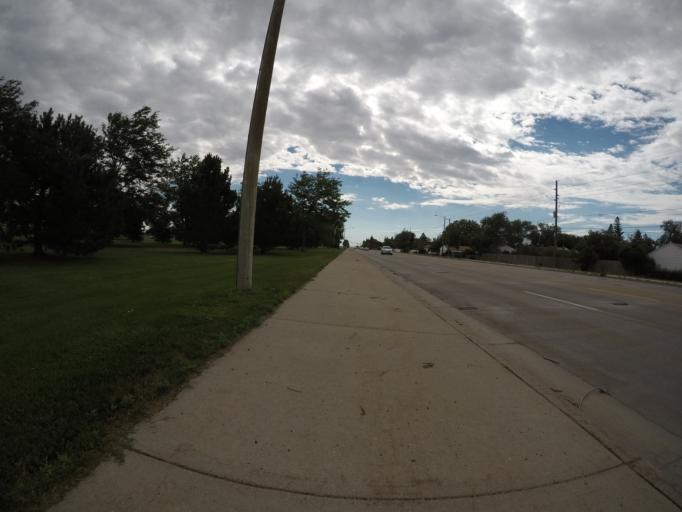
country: US
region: Wyoming
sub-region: Laramie County
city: Fox Farm-College
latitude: 41.1458
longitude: -104.7840
